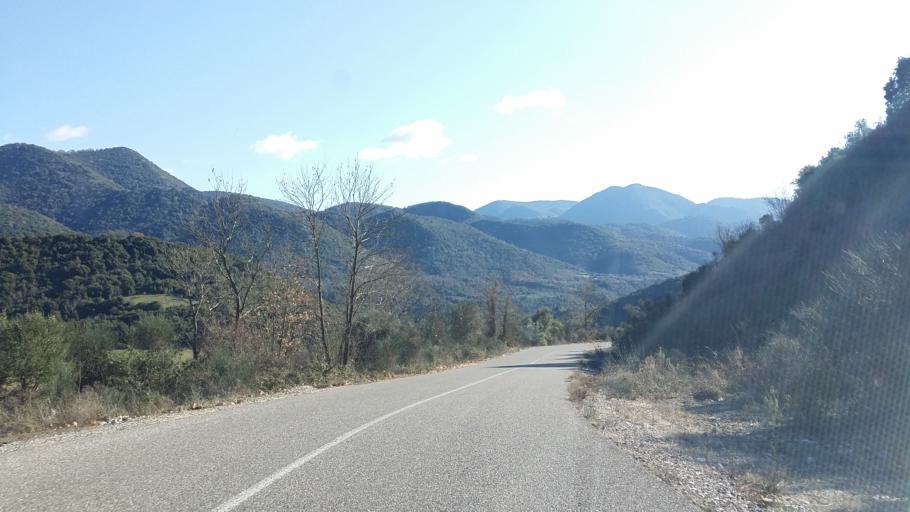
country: GR
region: Central Greece
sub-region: Nomos Evrytanias
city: Kerasochori
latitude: 38.9984
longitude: 21.5551
